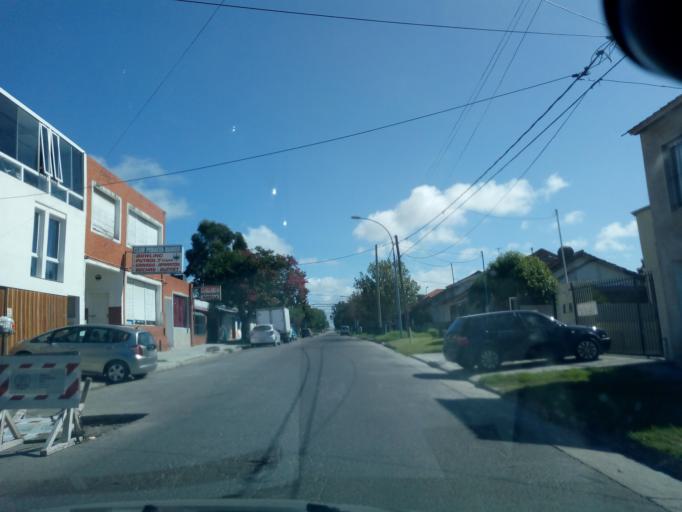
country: AR
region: Buenos Aires
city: Mar del Plata
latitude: -38.0650
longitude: -57.5518
